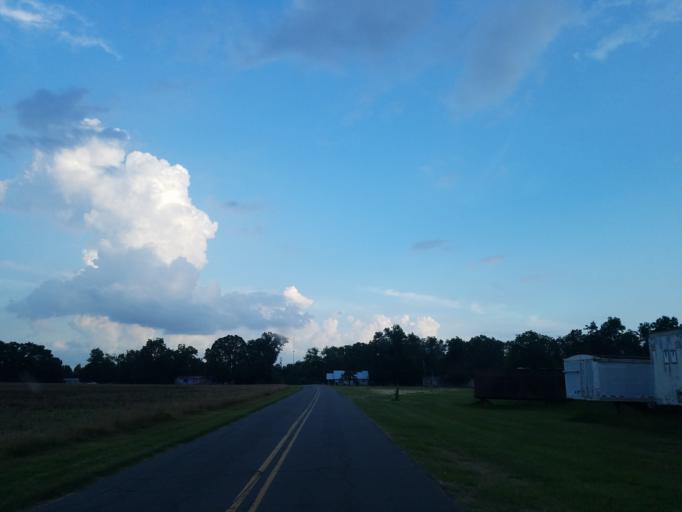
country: US
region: Georgia
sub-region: Dooly County
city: Unadilla
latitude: 32.1932
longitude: -83.7586
